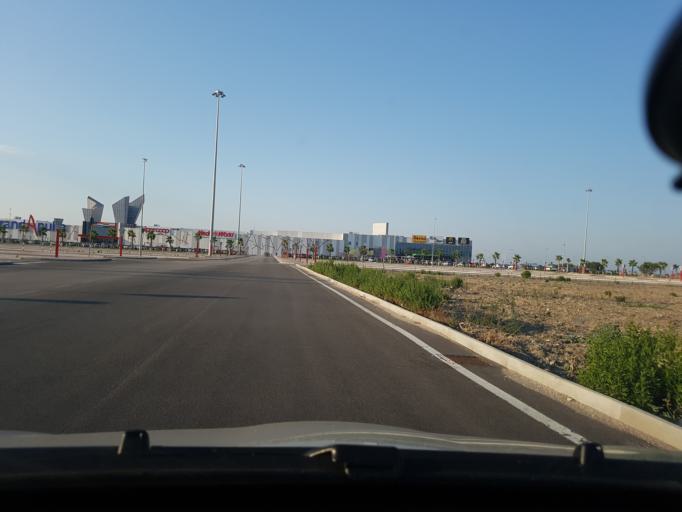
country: IT
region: Apulia
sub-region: Provincia di Foggia
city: Carapelle
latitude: 41.4130
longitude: 15.6514
